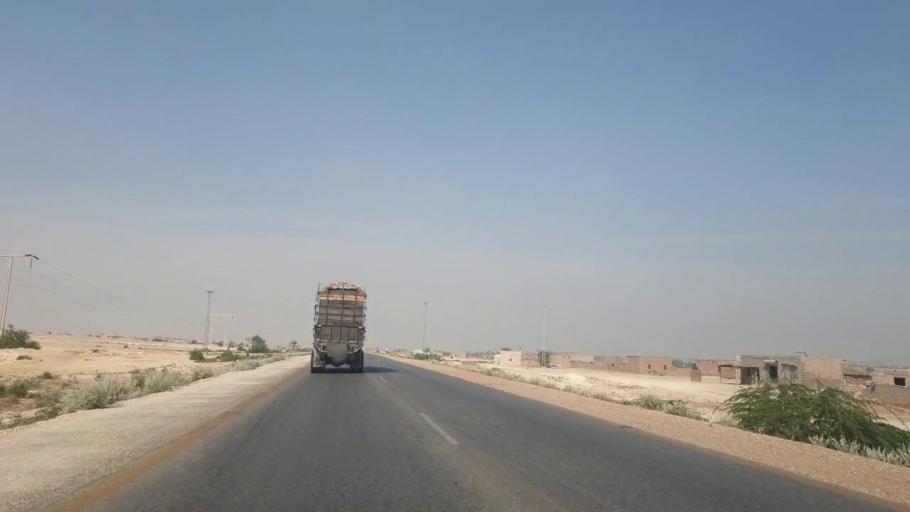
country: PK
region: Sindh
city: Hala
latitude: 25.7783
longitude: 68.2843
